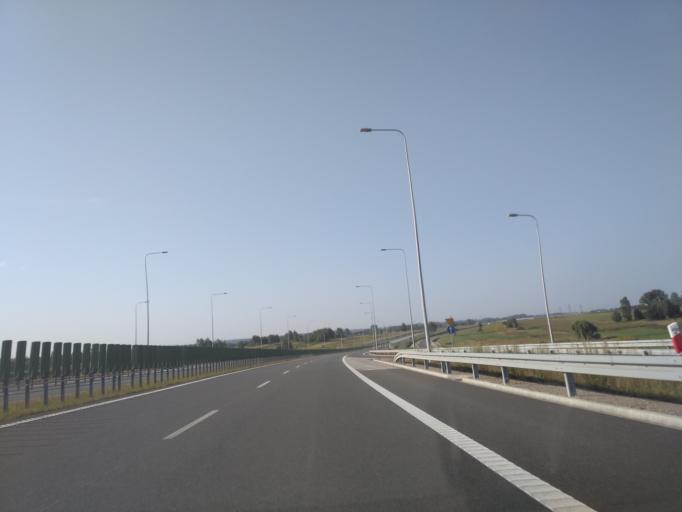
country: PL
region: Subcarpathian Voivodeship
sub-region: Powiat rzeszowski
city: Sokolow Malopolski
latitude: 50.2281
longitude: 22.1394
